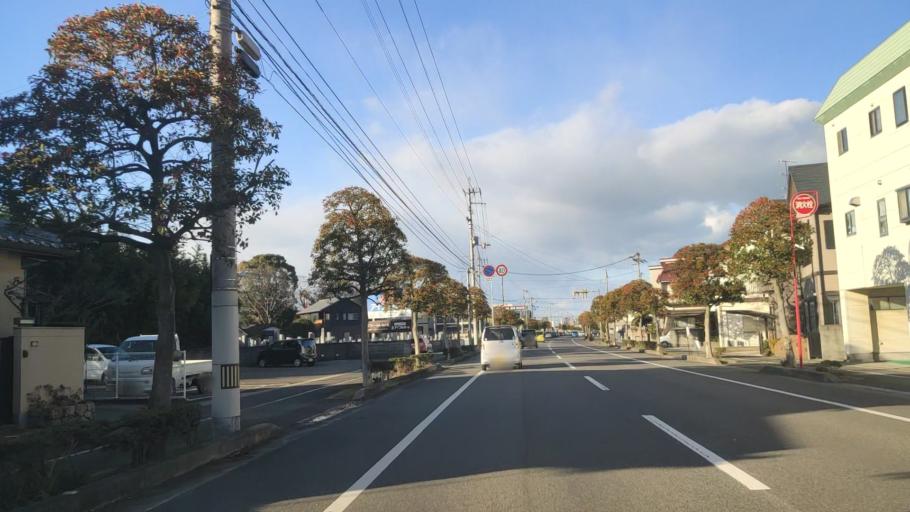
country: JP
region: Ehime
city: Saijo
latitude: 33.9219
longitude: 133.1844
